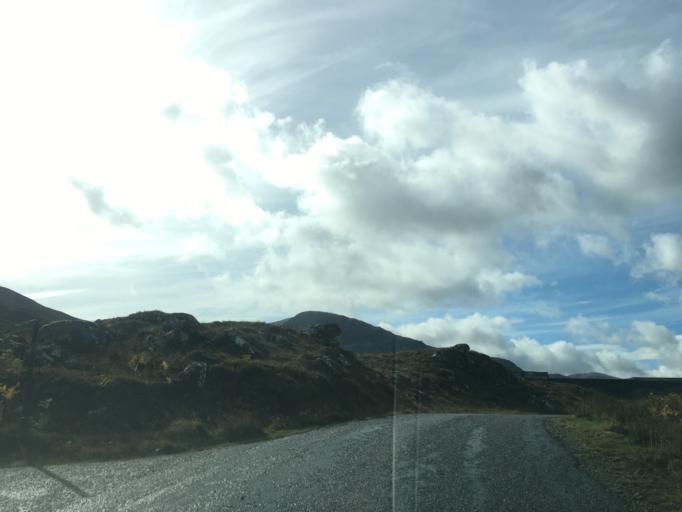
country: GB
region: Scotland
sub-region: Highland
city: Spean Bridge
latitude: 57.3409
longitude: -4.9455
